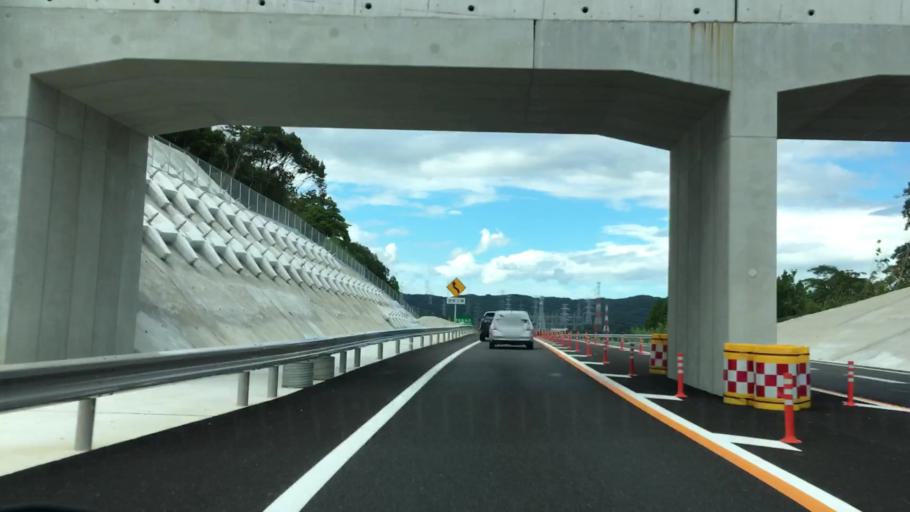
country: JP
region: Saga Prefecture
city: Imaricho-ko
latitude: 33.3318
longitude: 129.9279
